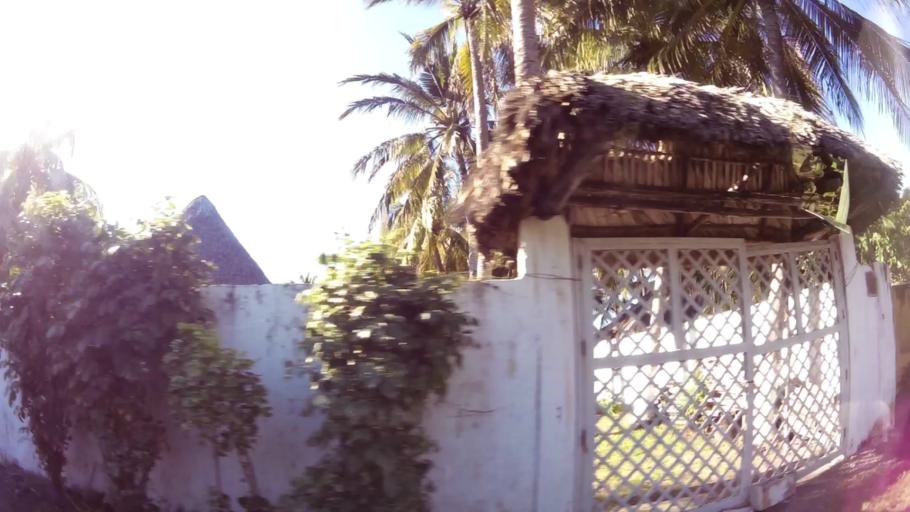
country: GT
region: Santa Rosa
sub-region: Municipio de Taxisco
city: Taxisco
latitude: 13.8919
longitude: -90.4888
